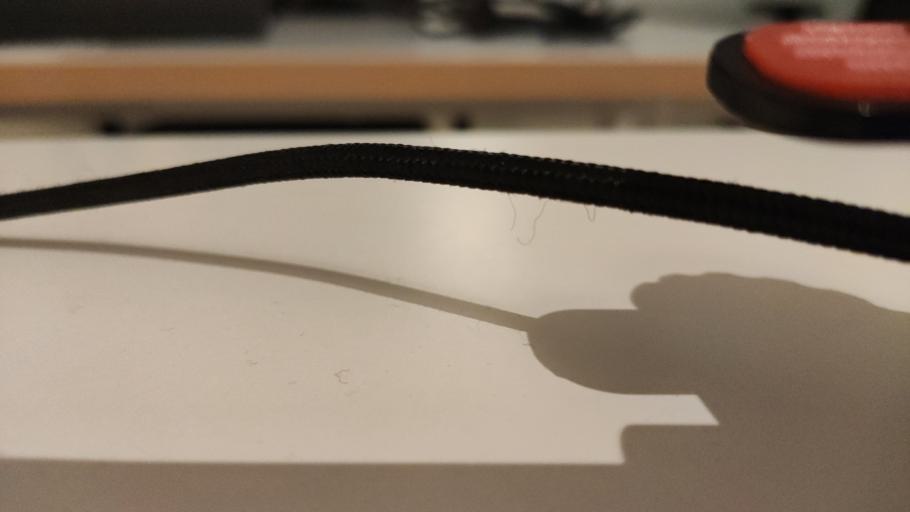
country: RU
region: Moskovskaya
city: Kurovskoye
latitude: 55.5814
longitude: 38.8895
